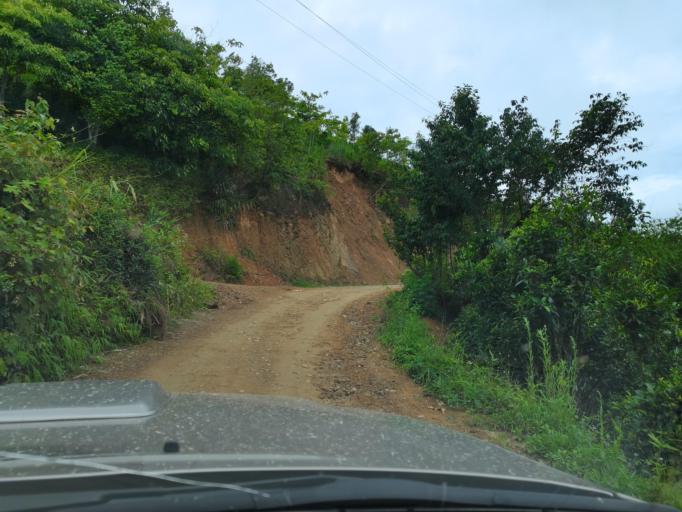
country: LA
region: Phongsali
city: Phongsali
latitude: 21.6458
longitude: 102.0932
